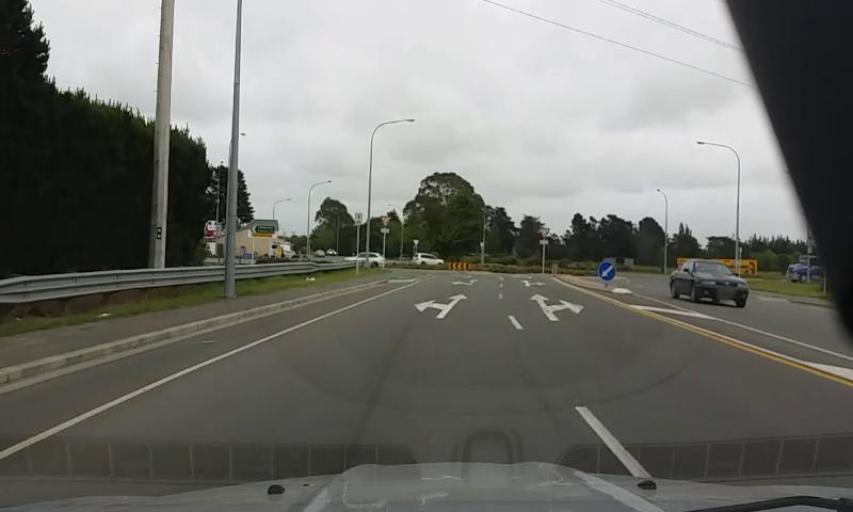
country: NZ
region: Canterbury
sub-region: Selwyn District
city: Prebbleton
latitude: -43.5129
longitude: 172.5100
